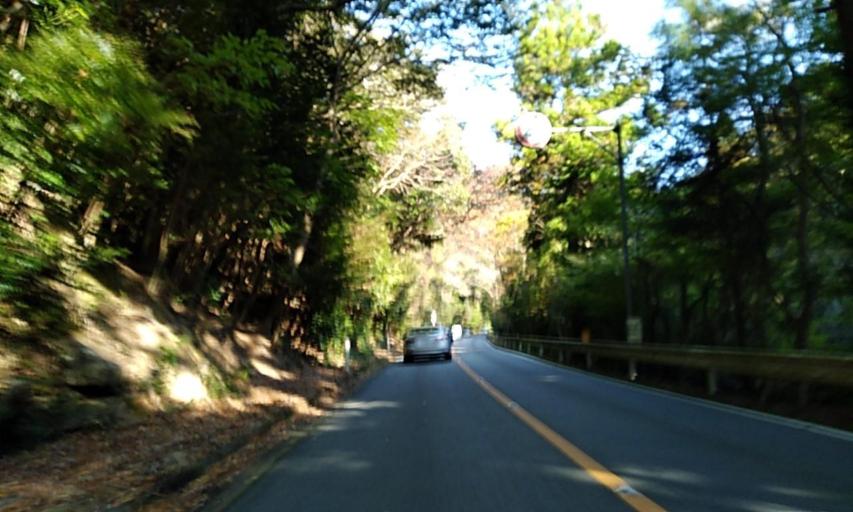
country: JP
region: Mie
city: Ise
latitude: 34.4415
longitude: 136.7524
